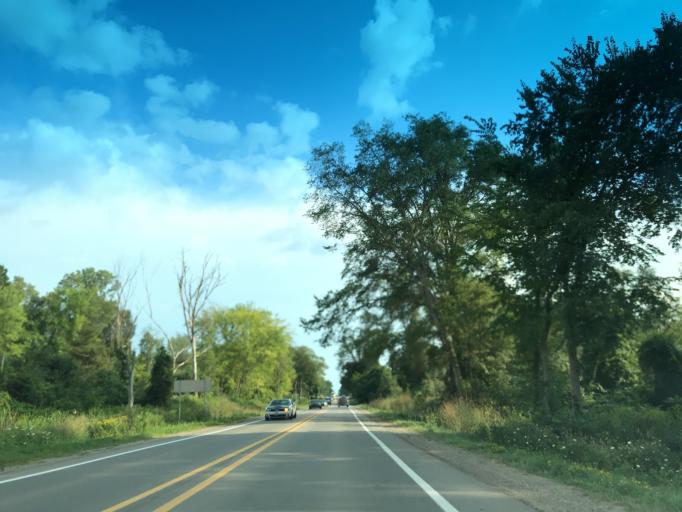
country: US
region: Michigan
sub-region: Oakland County
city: Milford
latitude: 42.5498
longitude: -83.6179
